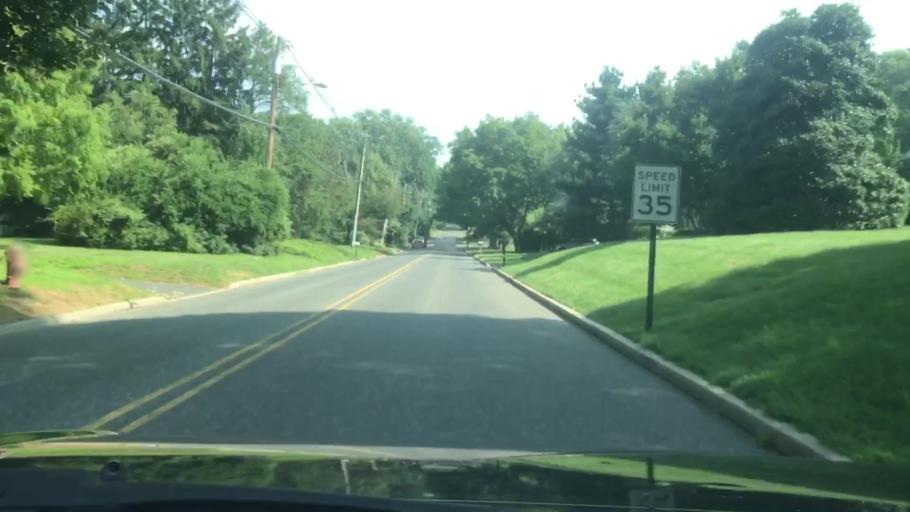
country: US
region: New Jersey
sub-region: Monmouth County
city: Little Silver
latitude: 40.3466
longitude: -74.0498
